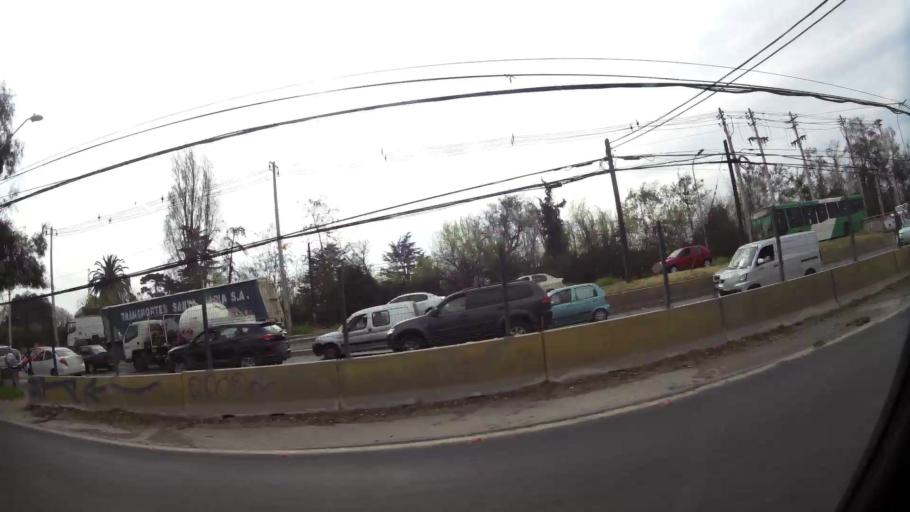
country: CL
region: Santiago Metropolitan
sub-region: Provincia de Maipo
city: San Bernardo
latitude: -33.5288
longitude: -70.7587
